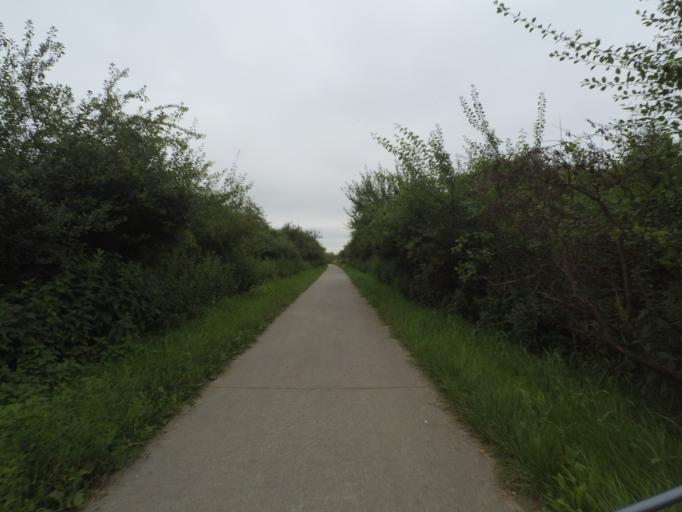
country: NL
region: Flevoland
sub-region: Gemeente Almere
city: Almere Stad
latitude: 52.4245
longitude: 5.2736
